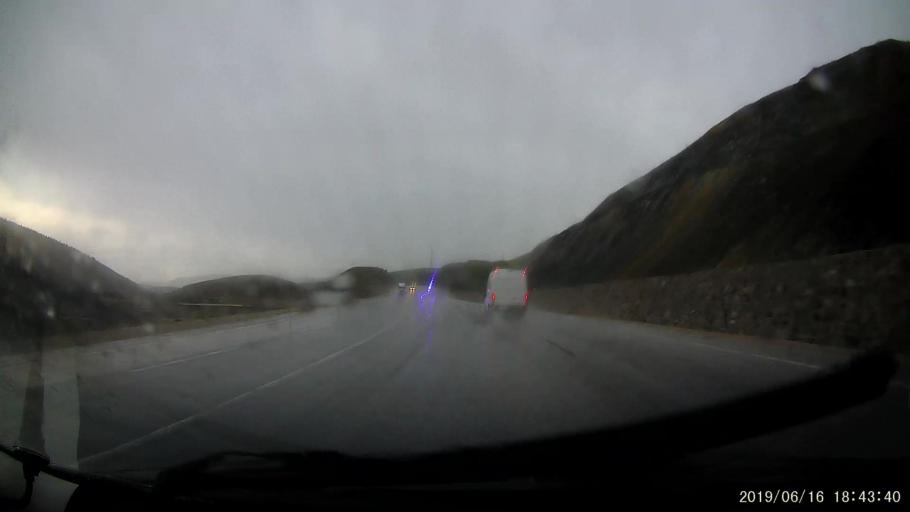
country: TR
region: Erzincan
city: Doganbeyli
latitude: 39.8718
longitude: 39.0889
